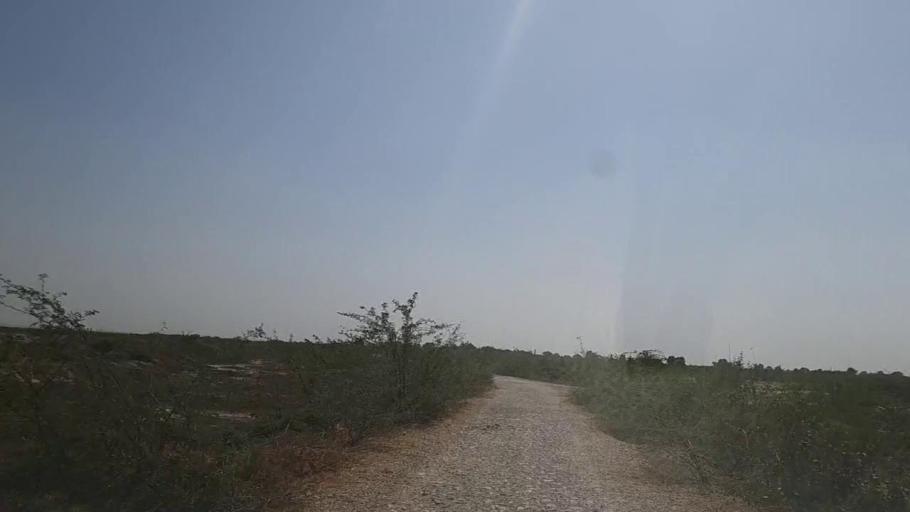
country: PK
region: Sindh
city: Naukot
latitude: 24.6334
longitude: 69.2723
